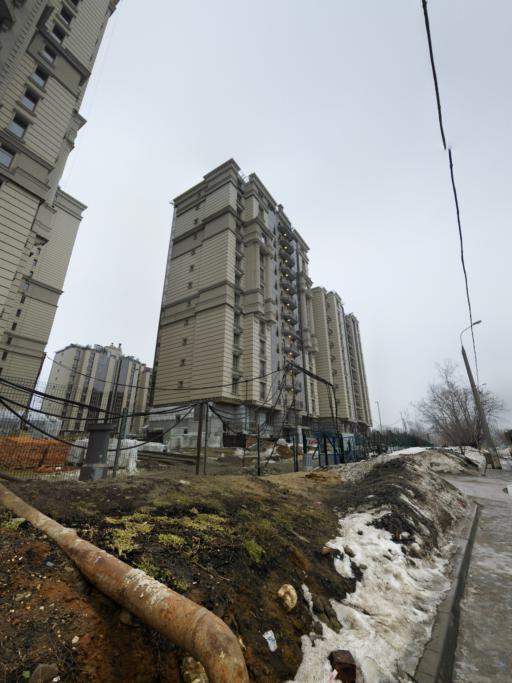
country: RU
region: Moscow
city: Metrogorodok
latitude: 55.7946
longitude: 37.7717
